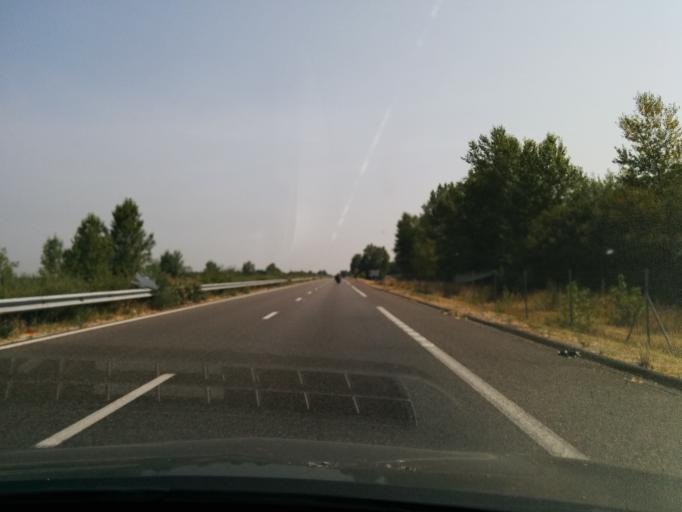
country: FR
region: Midi-Pyrenees
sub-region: Departement du Tarn
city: Lisle-sur-Tarn
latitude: 43.8266
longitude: 1.8226
